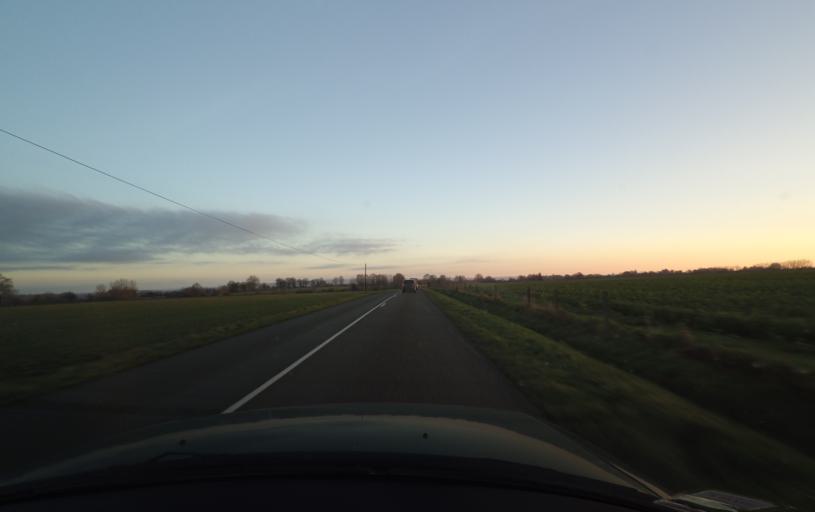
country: FR
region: Pays de la Loire
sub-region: Departement de la Mayenne
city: Bais
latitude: 48.2964
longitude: -0.3532
